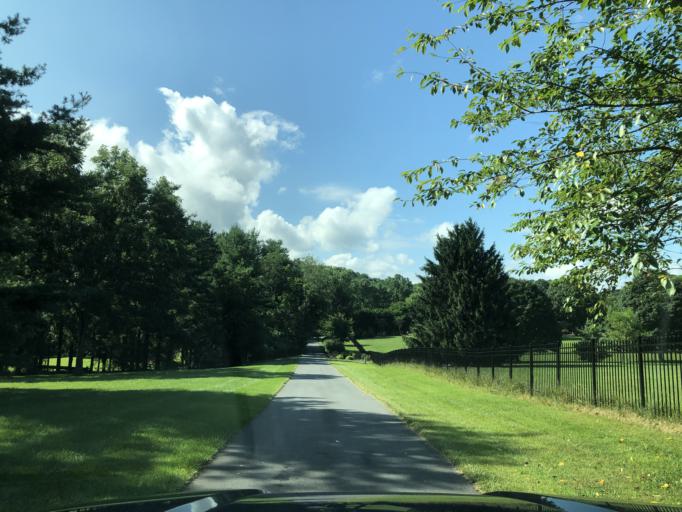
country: US
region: Maryland
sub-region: Howard County
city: Highland
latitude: 39.1909
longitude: -76.9379
